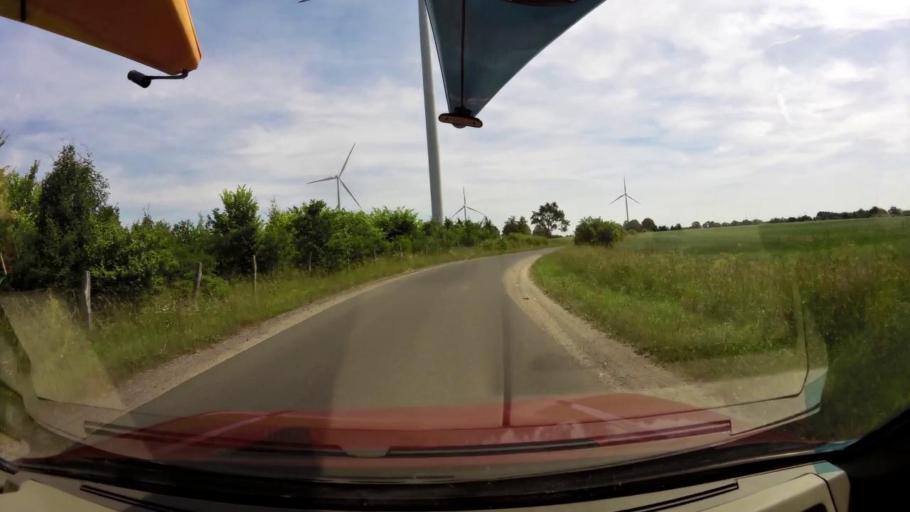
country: PL
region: West Pomeranian Voivodeship
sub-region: Powiat slawienski
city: Darlowo
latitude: 54.3125
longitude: 16.4709
